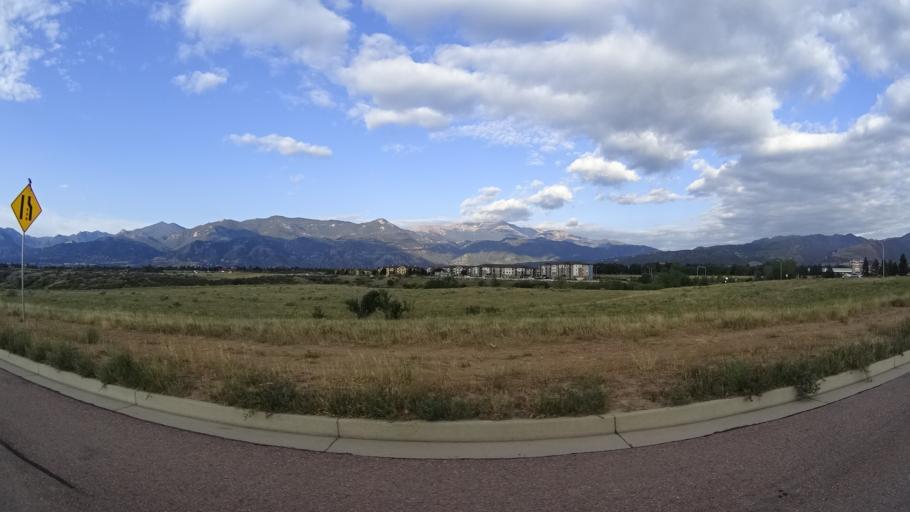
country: US
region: Colorado
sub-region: El Paso County
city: Colorado Springs
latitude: 38.8754
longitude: -104.8467
